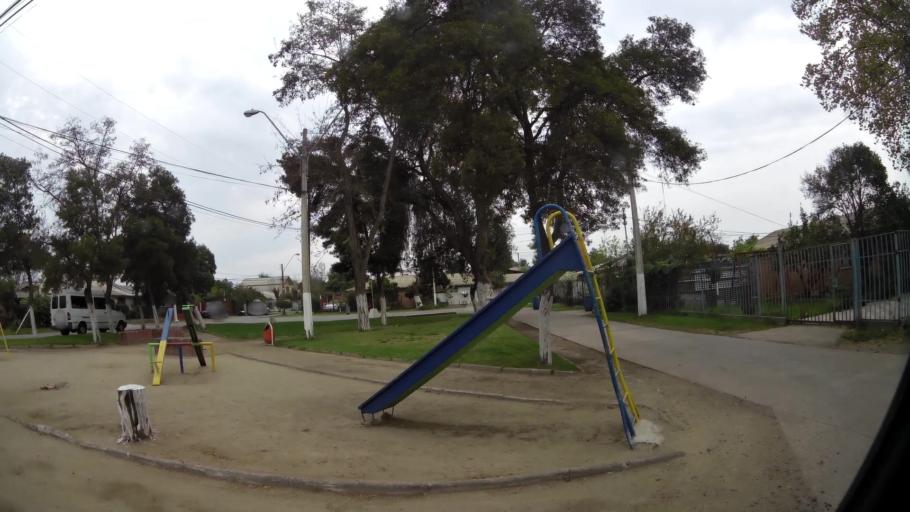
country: CL
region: Santiago Metropolitan
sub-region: Provincia de Santiago
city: Lo Prado
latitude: -33.4996
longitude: -70.7659
